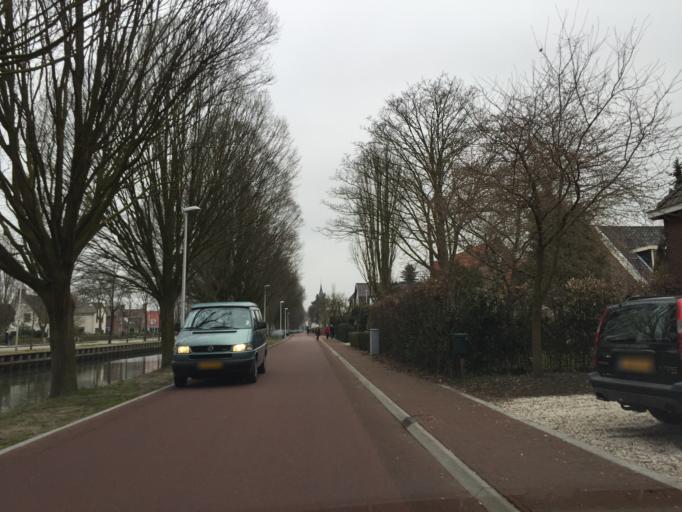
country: NL
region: Utrecht
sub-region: Stichtse Vecht
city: Maarssen
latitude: 52.0821
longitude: 5.0422
